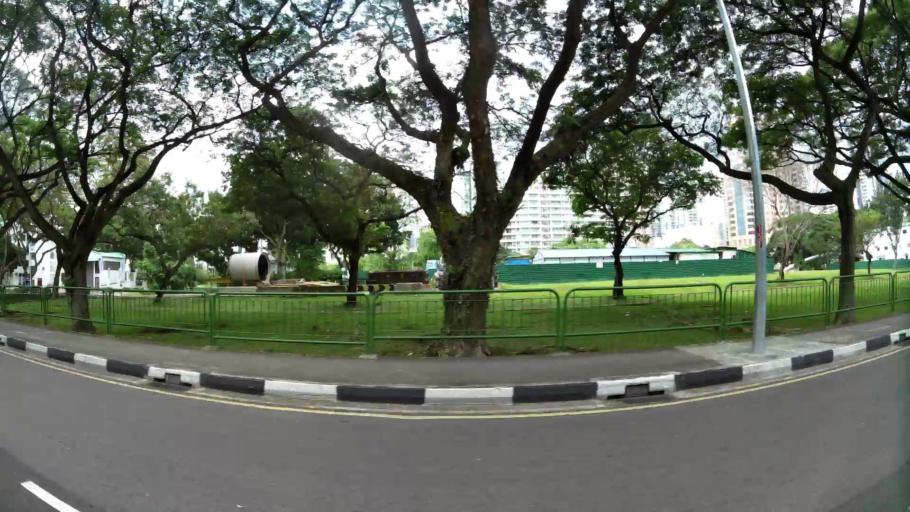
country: SG
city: Singapore
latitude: 1.2906
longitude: 103.8301
